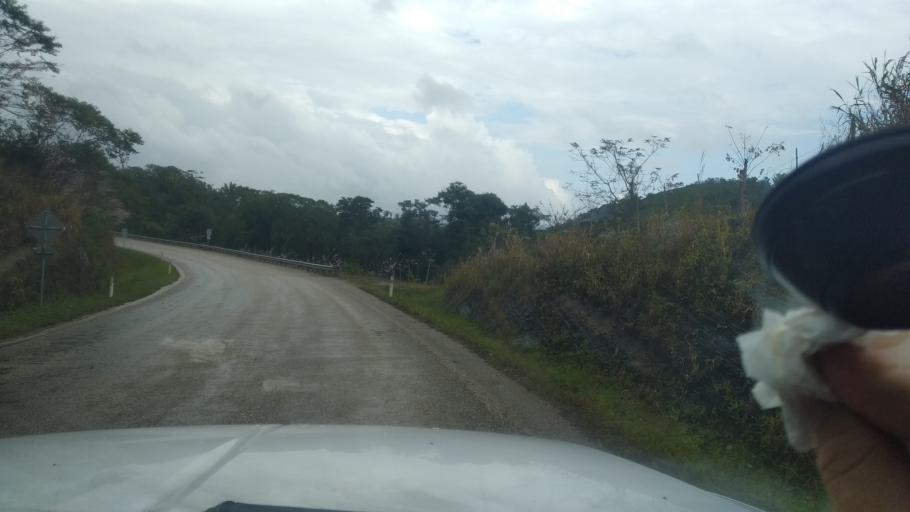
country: GT
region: Peten
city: San Luis
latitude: 16.1866
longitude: -89.1913
